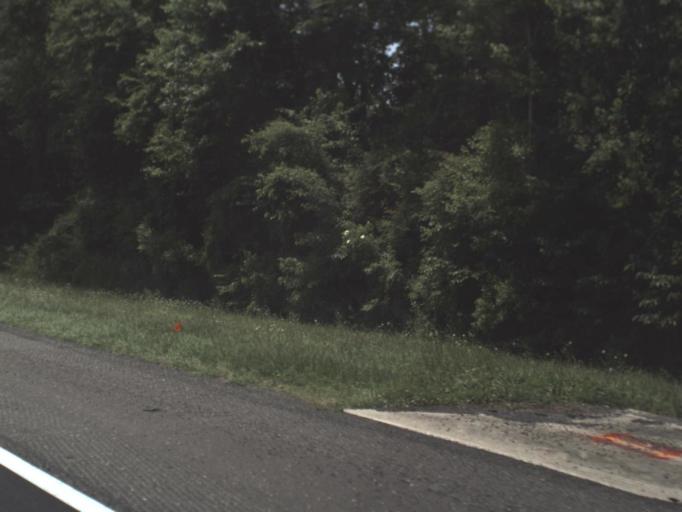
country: US
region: Florida
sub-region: Nassau County
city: Yulee
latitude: 30.5252
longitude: -81.6361
